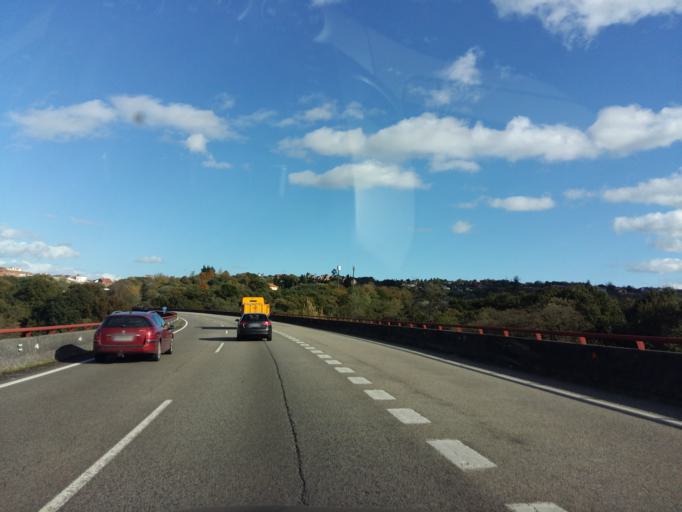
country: ES
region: Asturias
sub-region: Province of Asturias
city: Oviedo
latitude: 43.3454
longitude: -5.8600
